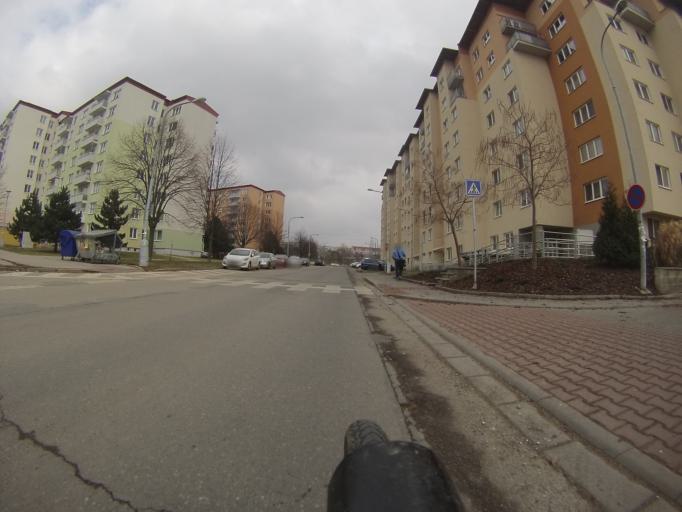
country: CZ
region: South Moravian
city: Bilovice nad Svitavou
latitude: 49.2032
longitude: 16.6702
